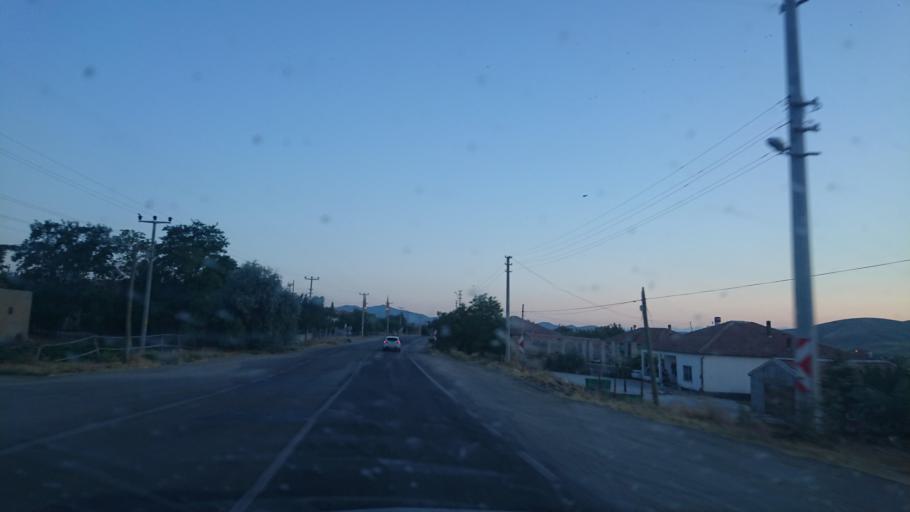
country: TR
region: Aksaray
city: Balci
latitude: 38.7947
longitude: 34.1258
